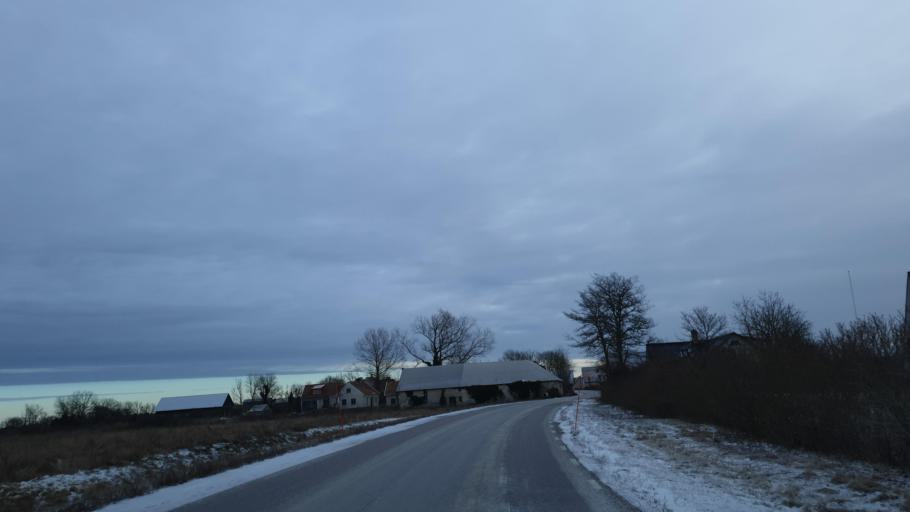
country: SE
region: Gotland
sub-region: Gotland
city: Slite
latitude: 57.4229
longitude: 18.9033
